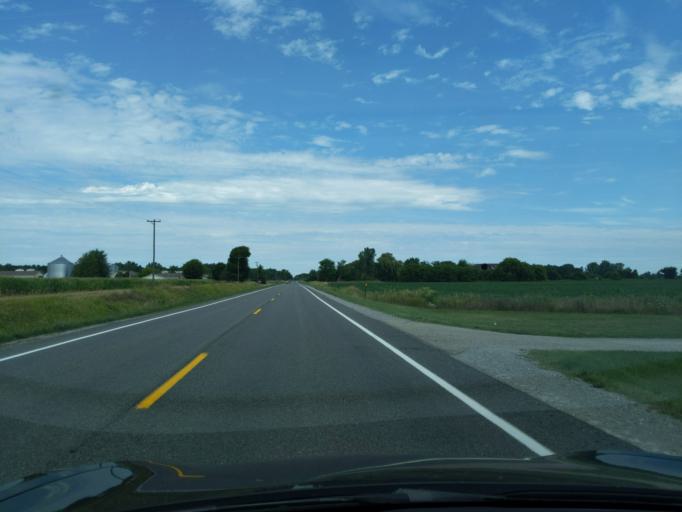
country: US
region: Michigan
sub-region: Gratiot County
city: Breckenridge
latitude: 43.5045
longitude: -84.3698
